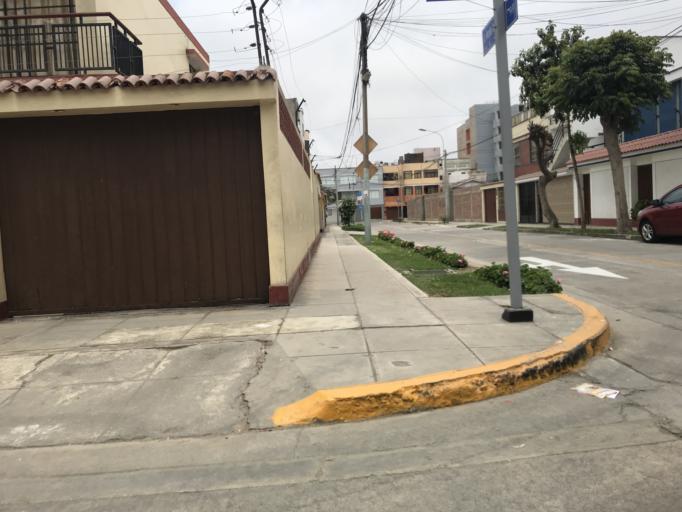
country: PE
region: Callao
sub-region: Callao
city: Callao
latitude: -12.0798
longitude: -77.0781
